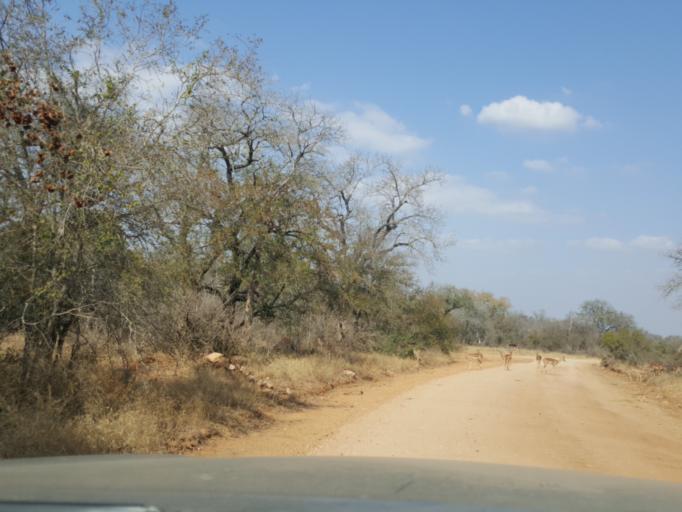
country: ZA
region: Mpumalanga
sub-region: Ehlanzeni District
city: Komatipoort
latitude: -25.2876
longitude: 31.7709
